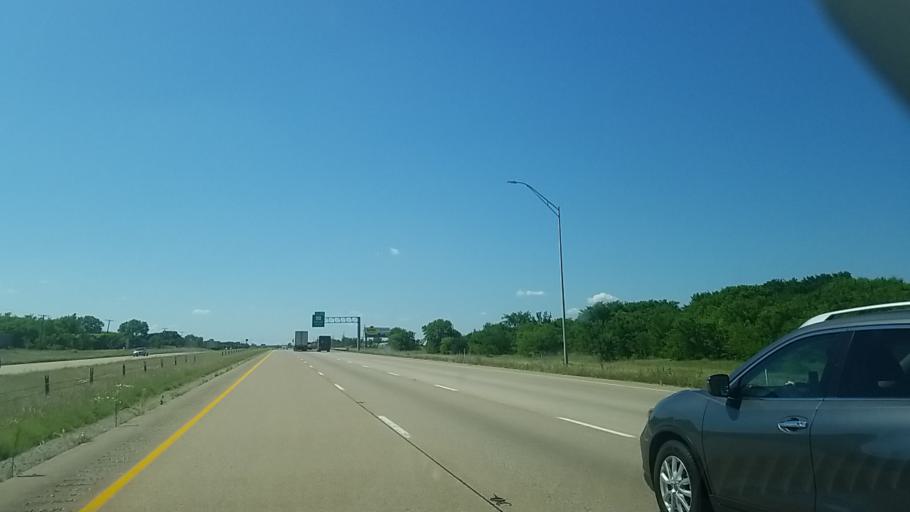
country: US
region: Texas
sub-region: Ellis County
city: Ennis
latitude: 32.3645
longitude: -96.6362
